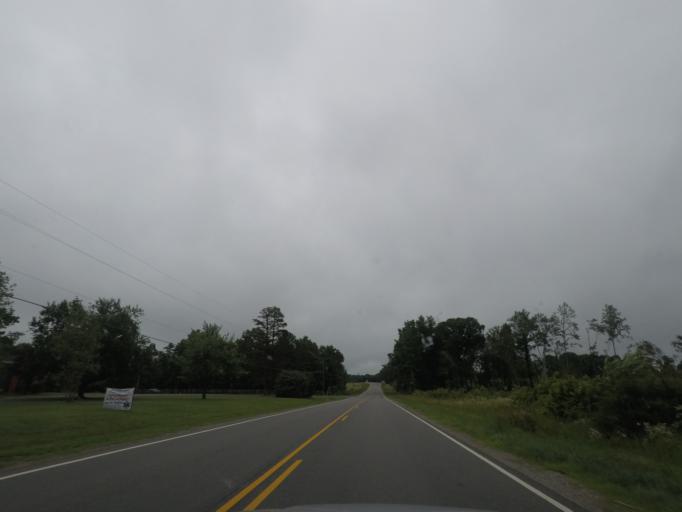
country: US
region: Virginia
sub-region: Fluvanna County
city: Weber City
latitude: 37.6339
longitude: -78.3629
